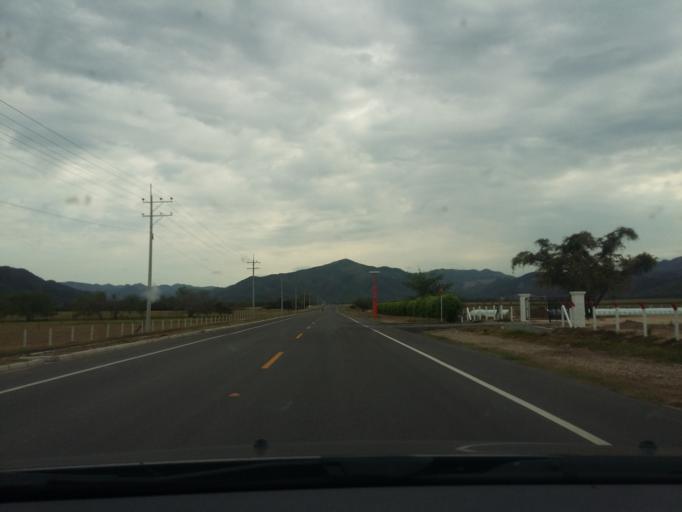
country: CO
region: Cundinamarca
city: Narino
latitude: 4.3757
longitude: -74.8387
